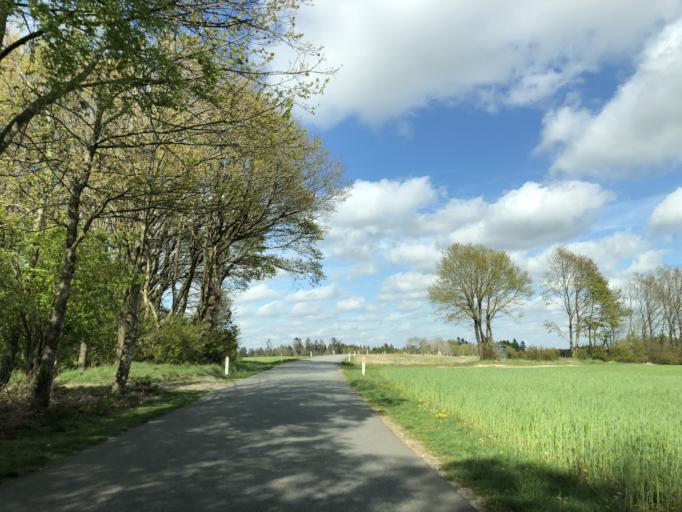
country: DK
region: Central Jutland
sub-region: Herning Kommune
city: Avlum
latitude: 56.3031
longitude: 8.7216
